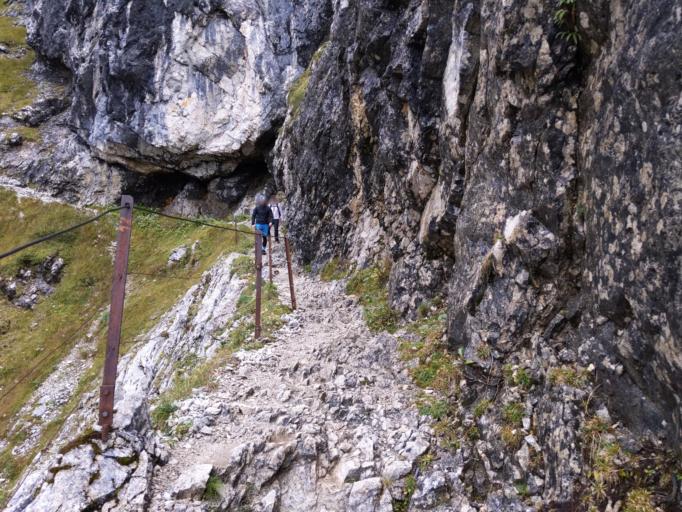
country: DE
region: Bavaria
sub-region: Upper Bavaria
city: Grainau
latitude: 47.4412
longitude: 11.0423
